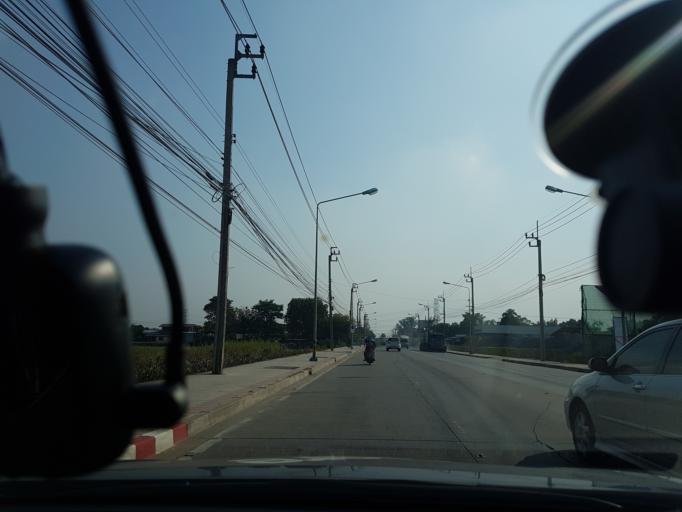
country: TH
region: Bangkok
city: Khlong Sam Wa
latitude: 13.8836
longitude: 100.7223
